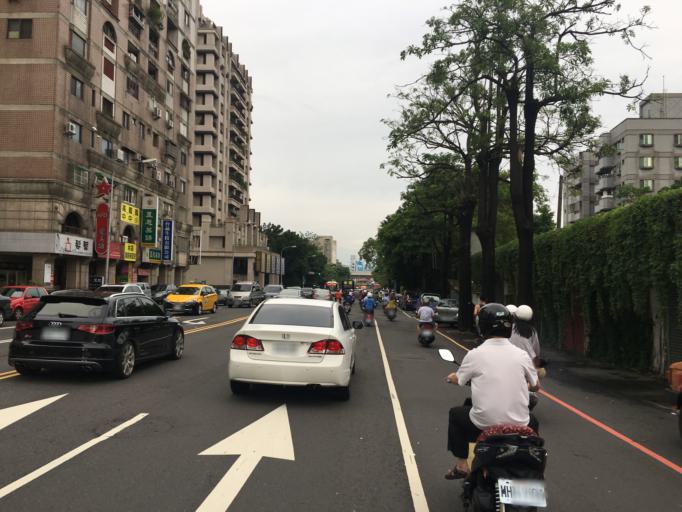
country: TW
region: Taiwan
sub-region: Taichung City
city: Taichung
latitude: 24.1358
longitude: 120.6727
